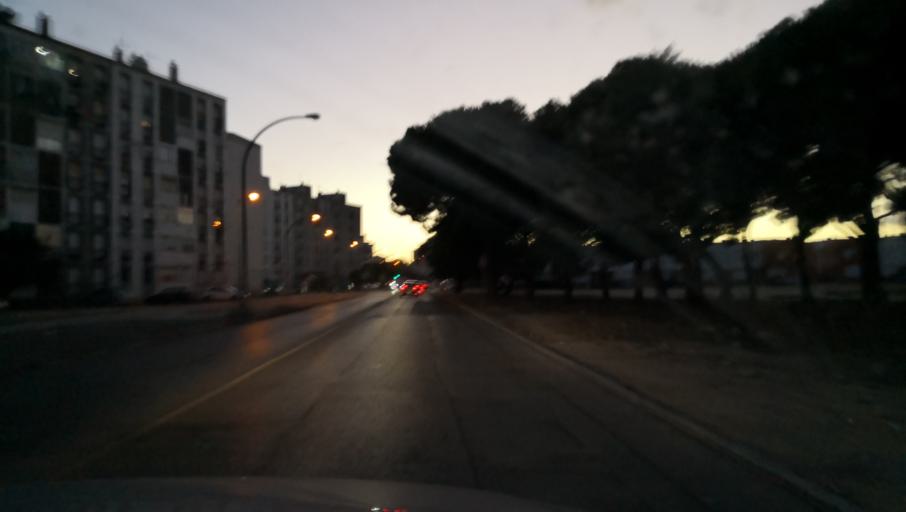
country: PT
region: Setubal
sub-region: Moita
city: Alhos Vedros
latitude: 38.6518
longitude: -9.0380
